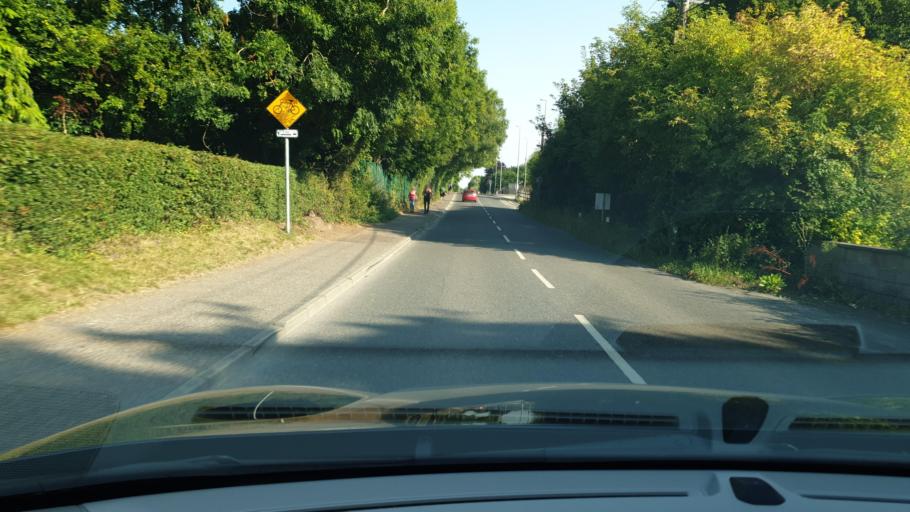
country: IE
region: Leinster
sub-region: An Mhi
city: Navan
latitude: 53.6640
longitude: -6.6955
